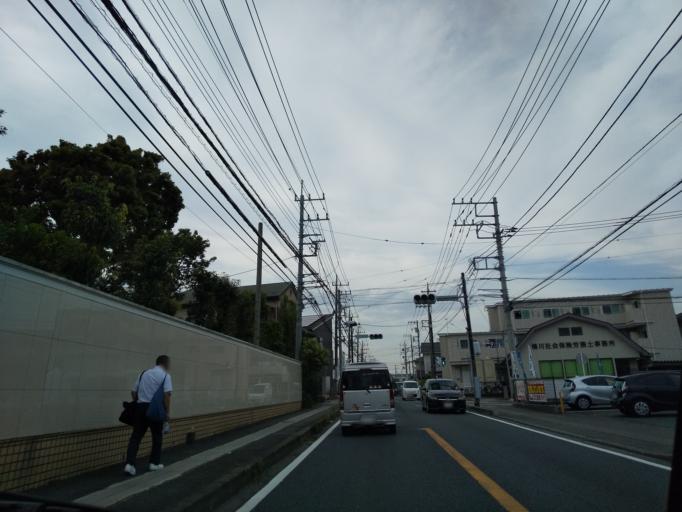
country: JP
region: Kanagawa
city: Zama
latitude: 35.4920
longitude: 139.3398
